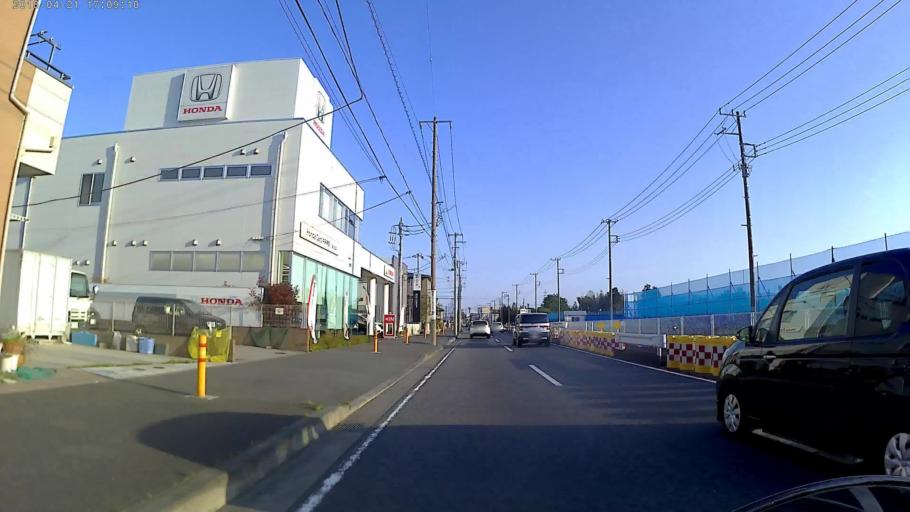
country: JP
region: Kanagawa
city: Fujisawa
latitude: 35.3991
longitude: 139.4425
